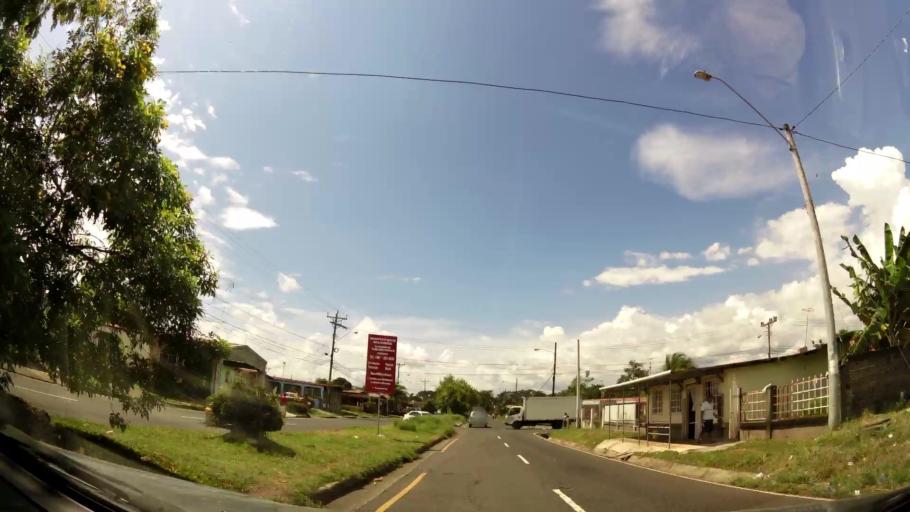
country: PA
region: Panama
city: Nuevo Arraijan
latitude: 8.9148
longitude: -79.7083
